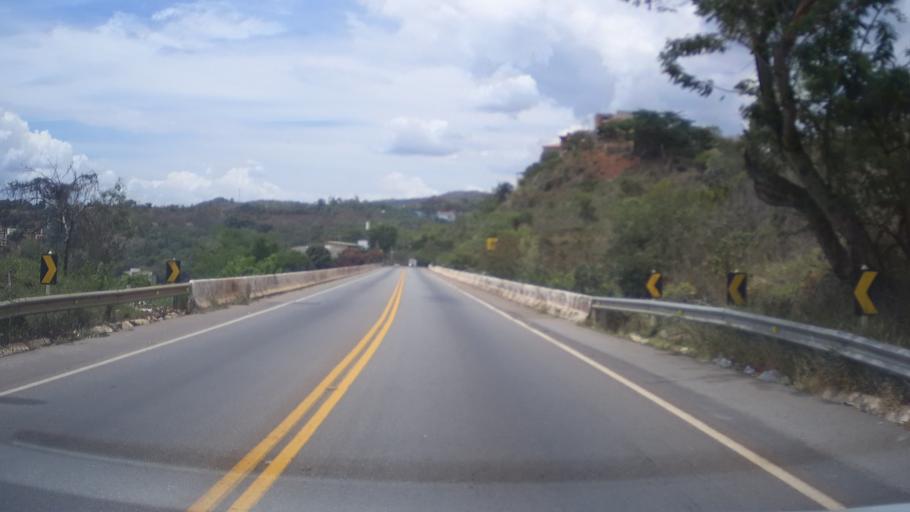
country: BR
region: Minas Gerais
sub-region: Nova Lima
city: Nova Lima
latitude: -20.0009
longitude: -43.8596
